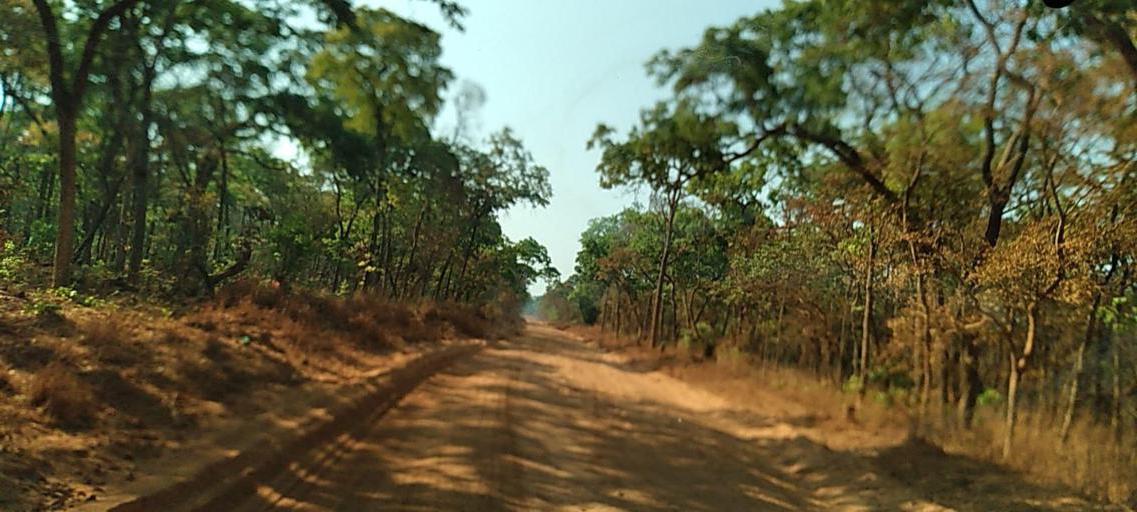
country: ZM
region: North-Western
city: Kasempa
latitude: -13.6433
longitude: 25.9985
